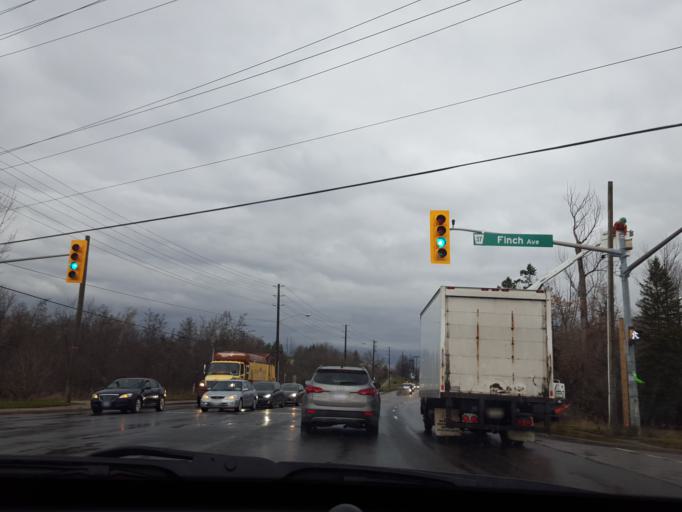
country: CA
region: Ontario
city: Ajax
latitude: 43.8499
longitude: -79.0752
